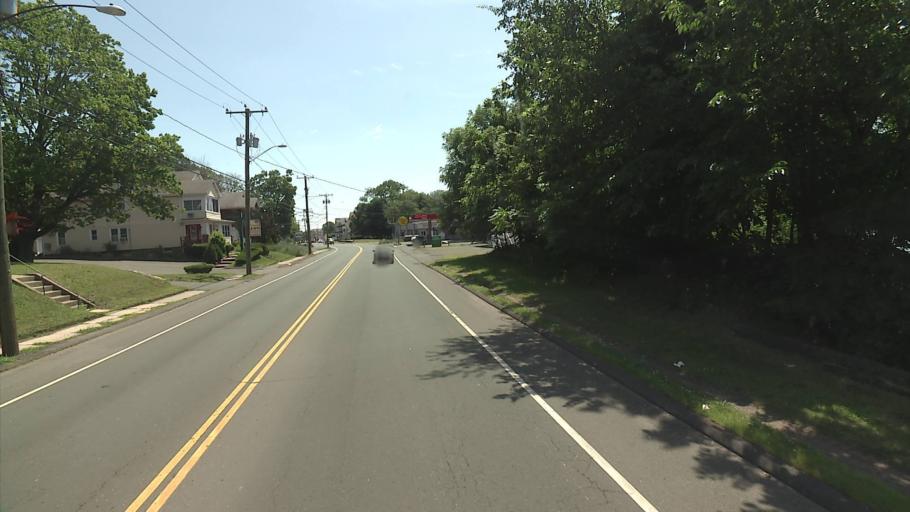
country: US
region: Connecticut
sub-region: Hartford County
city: New Britain
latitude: 41.6670
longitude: -72.8103
